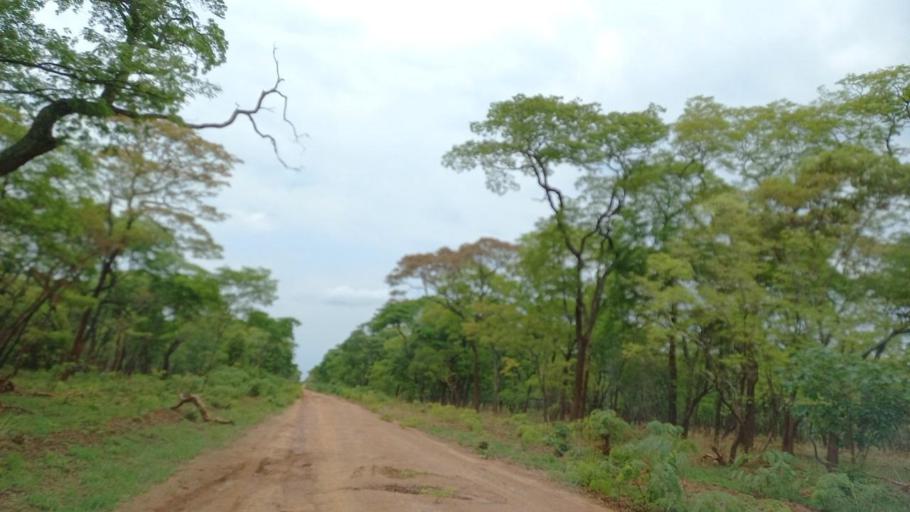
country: ZM
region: North-Western
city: Kalengwa
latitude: -13.6048
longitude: 24.9748
